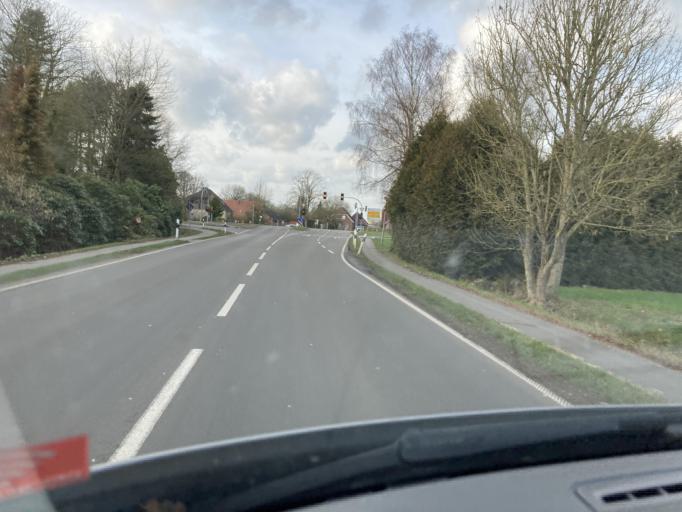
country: DE
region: Lower Saxony
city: Leer
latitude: 53.1766
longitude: 7.4883
